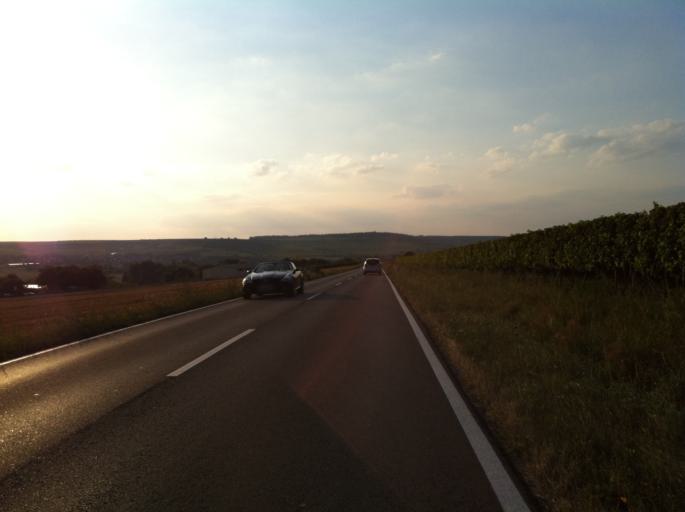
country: DE
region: Rheinland-Pfalz
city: Schwabenheim
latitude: 49.9206
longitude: 8.1103
